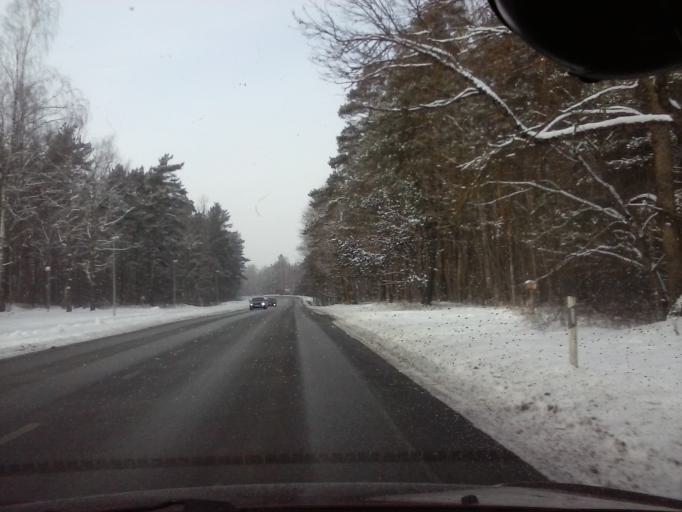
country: EE
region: Paernumaa
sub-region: Paikuse vald
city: Paikuse
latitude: 58.3757
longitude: 24.5676
